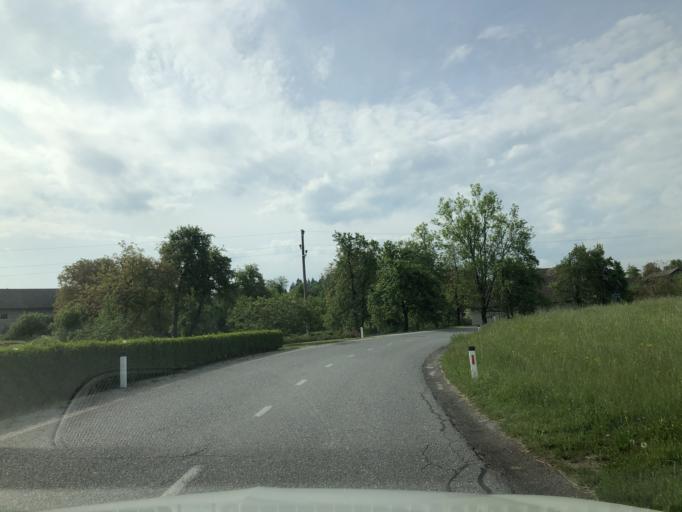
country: SI
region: Velike Lasce
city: Velike Lasce
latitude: 45.8103
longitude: 14.6263
